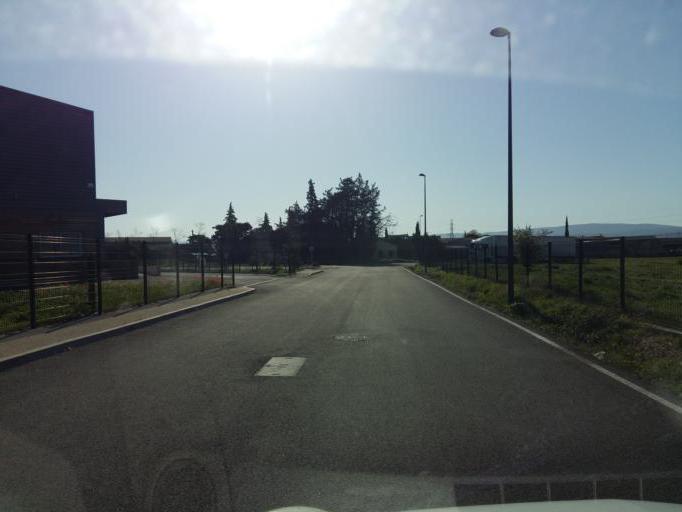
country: FR
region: Provence-Alpes-Cote d'Azur
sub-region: Departement du Vaucluse
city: Carpentras
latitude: 44.0357
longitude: 5.0366
